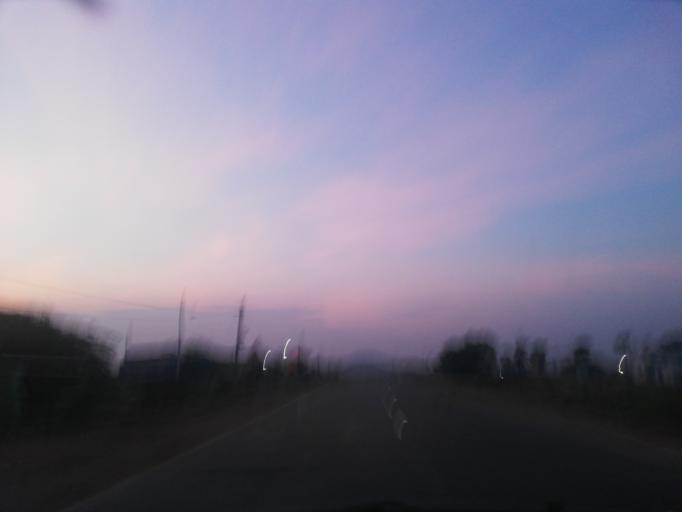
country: IN
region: Andhra Pradesh
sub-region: Guntur
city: Macherla
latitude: 16.6887
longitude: 79.2512
